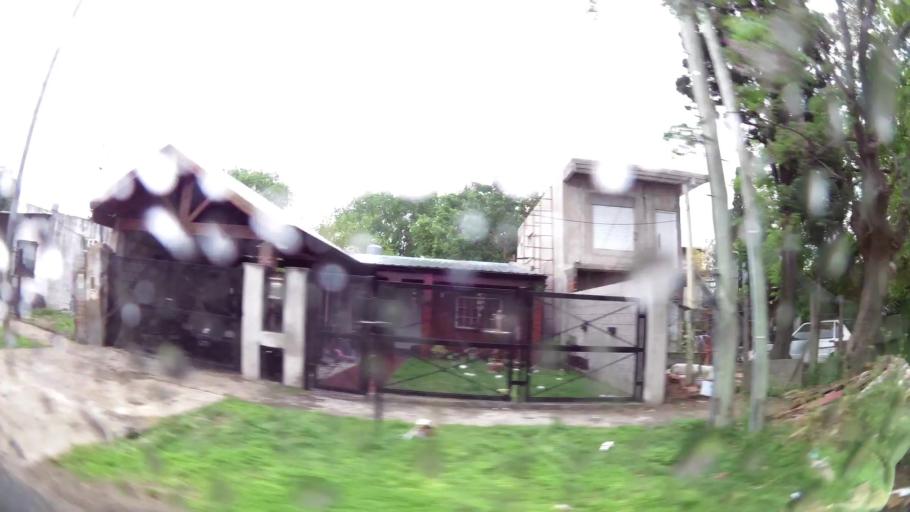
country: AR
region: Buenos Aires
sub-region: Partido de Quilmes
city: Quilmes
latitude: -34.7800
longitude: -58.2285
